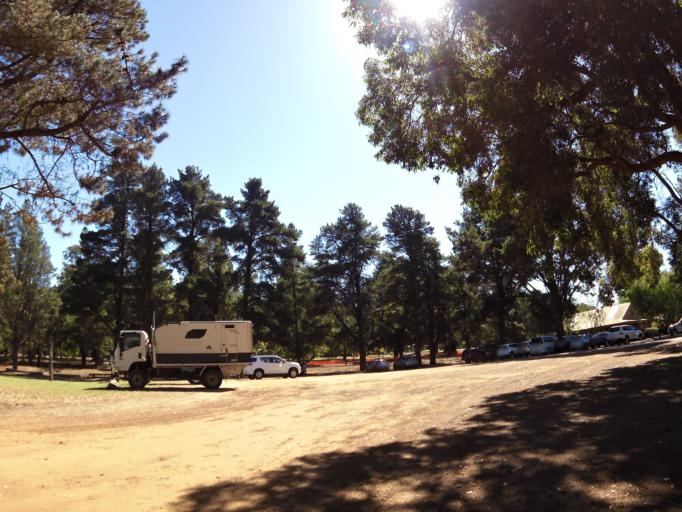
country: AU
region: Western Australia
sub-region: Waroona
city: Waroona
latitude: -32.7131
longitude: 116.0618
